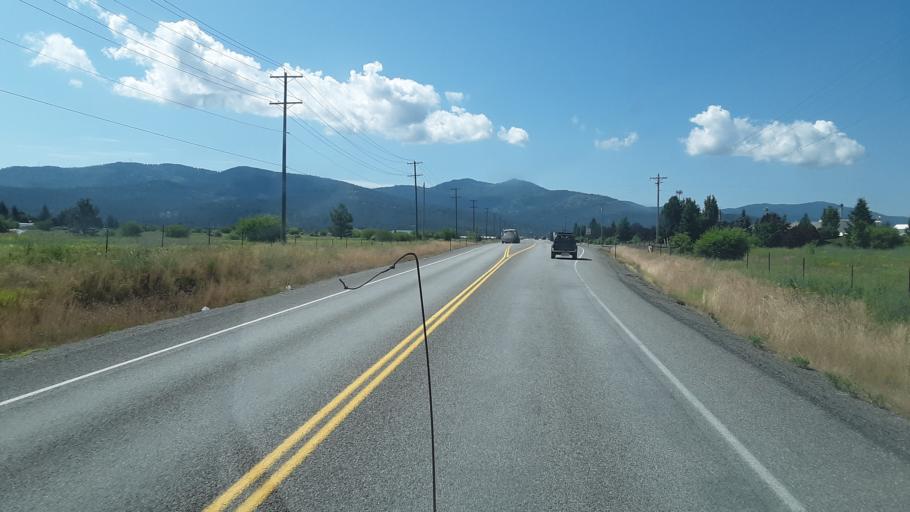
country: US
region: Idaho
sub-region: Kootenai County
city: Post Falls
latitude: 47.7233
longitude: -117.0016
